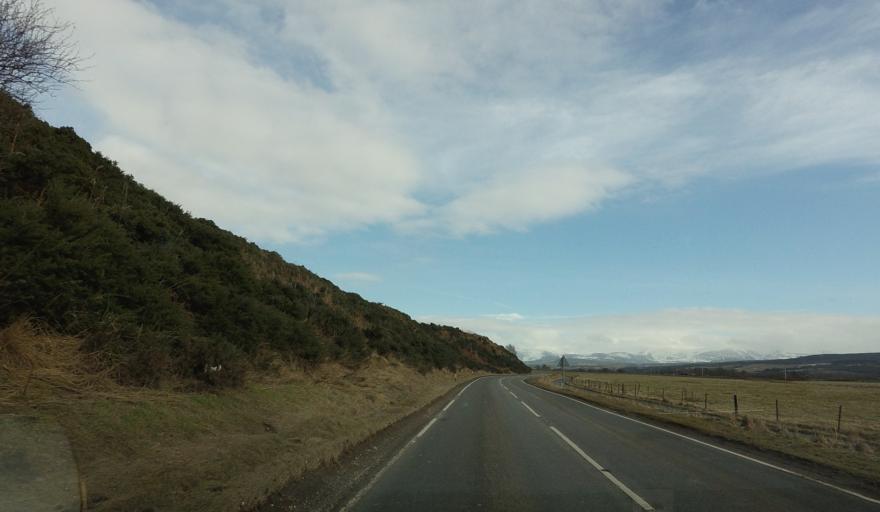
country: GB
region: Scotland
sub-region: Highland
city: Kingussie
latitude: 57.0752
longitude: -4.0841
